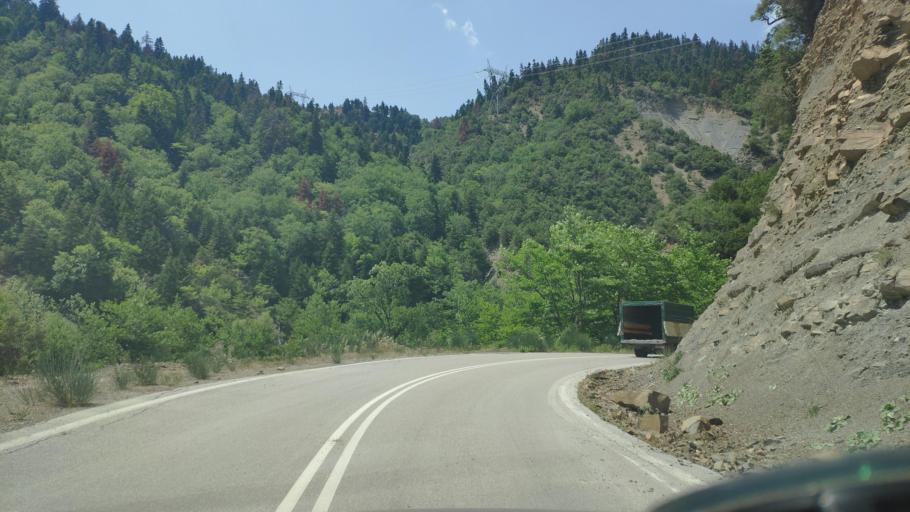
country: GR
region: Thessaly
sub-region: Nomos Kardhitsas
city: Anthiro
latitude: 39.2717
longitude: 21.3500
